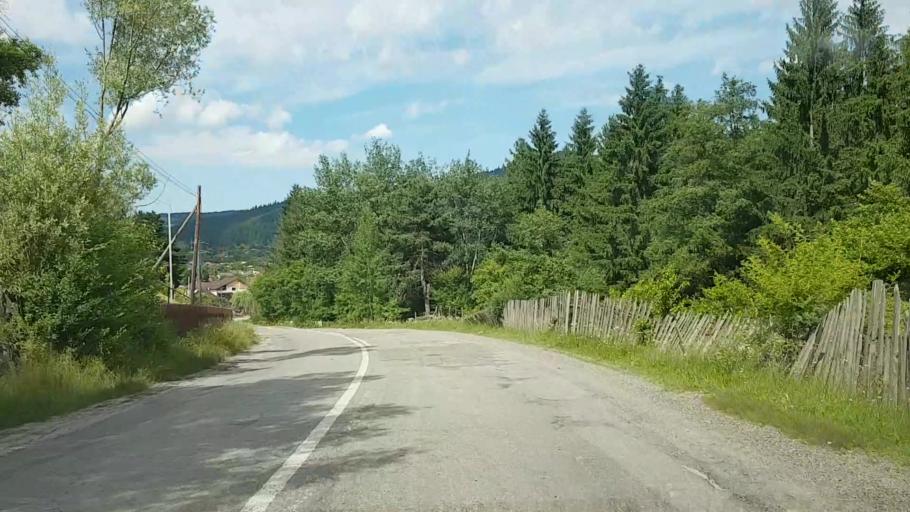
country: RO
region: Neamt
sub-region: Comuna Hangu
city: Hangu
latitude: 47.0578
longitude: 26.0314
